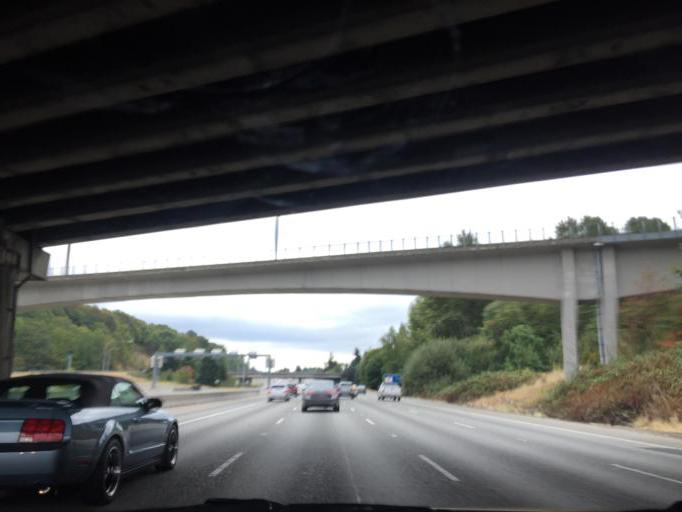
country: US
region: Washington
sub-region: King County
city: Riverton
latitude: 47.5078
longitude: -122.2817
